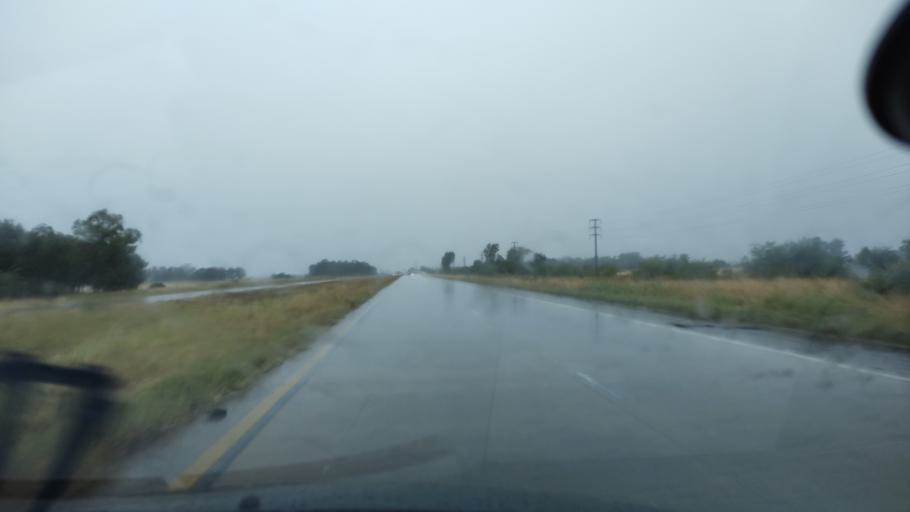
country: AR
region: Buenos Aires
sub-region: Partido de San Vicente
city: San Vicente
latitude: -35.0694
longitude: -58.5164
